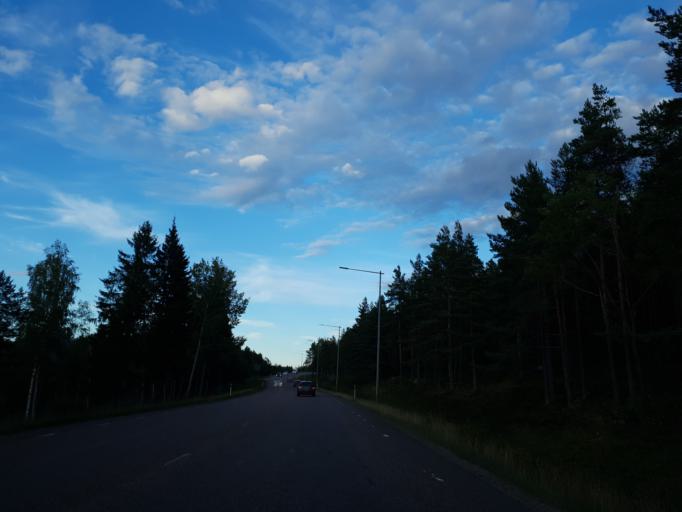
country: SE
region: Gaevleborg
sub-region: Soderhamns Kommun
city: Soderhamn
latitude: 61.2918
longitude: 17.0496
